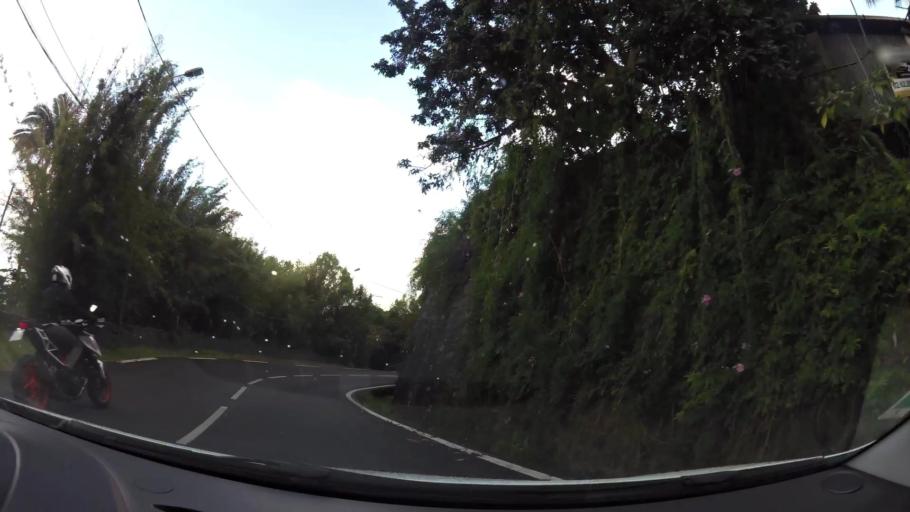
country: RE
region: Reunion
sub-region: Reunion
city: Saint-Denis
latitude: -20.9122
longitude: 55.4404
